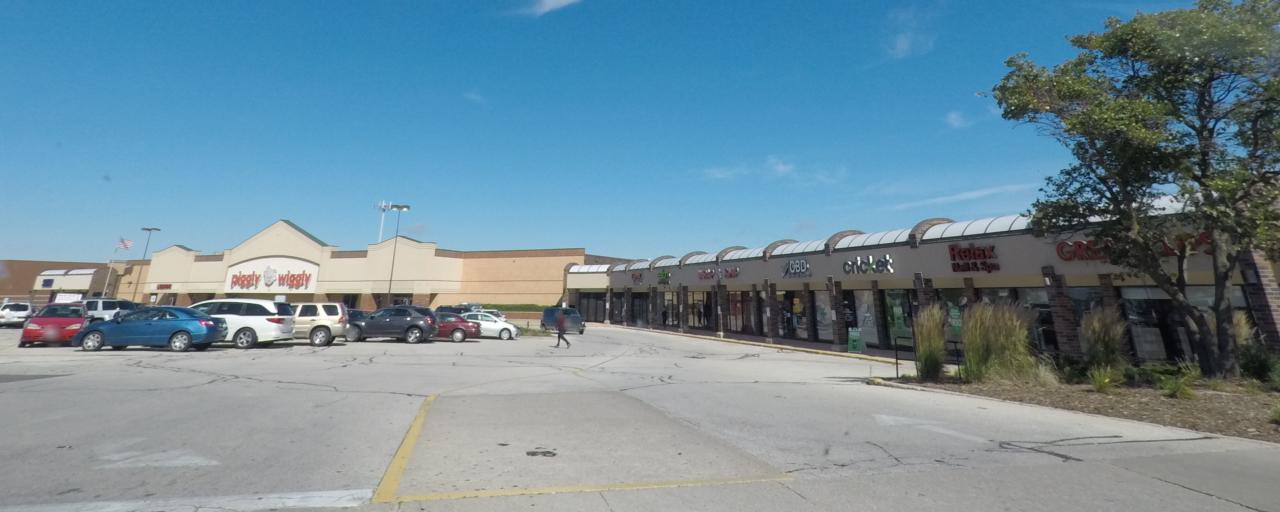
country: US
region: Wisconsin
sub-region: Milwaukee County
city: West Allis
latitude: 42.9962
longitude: -88.0428
